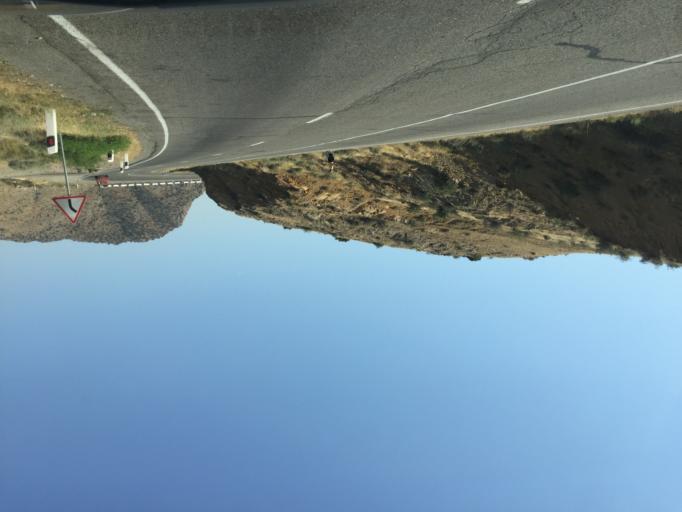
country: AM
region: Ararat
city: Zangakatun
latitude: 39.7938
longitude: 44.9524
